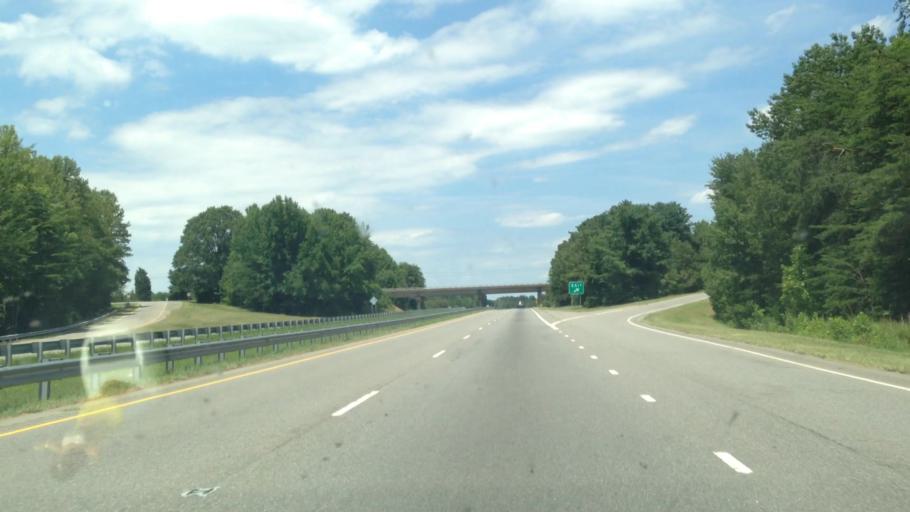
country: US
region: North Carolina
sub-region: Rockingham County
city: Stoneville
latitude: 36.4996
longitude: -79.9220
